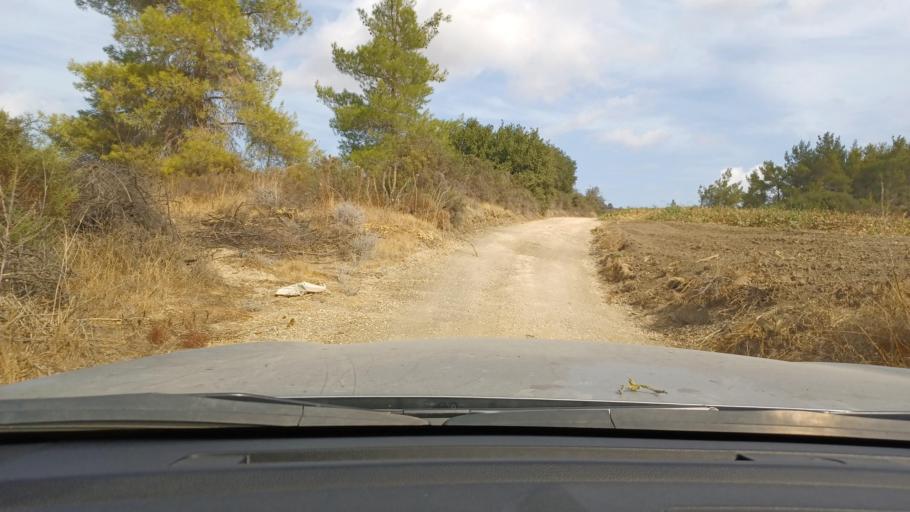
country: CY
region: Pafos
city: Polis
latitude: 35.0115
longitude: 32.5173
